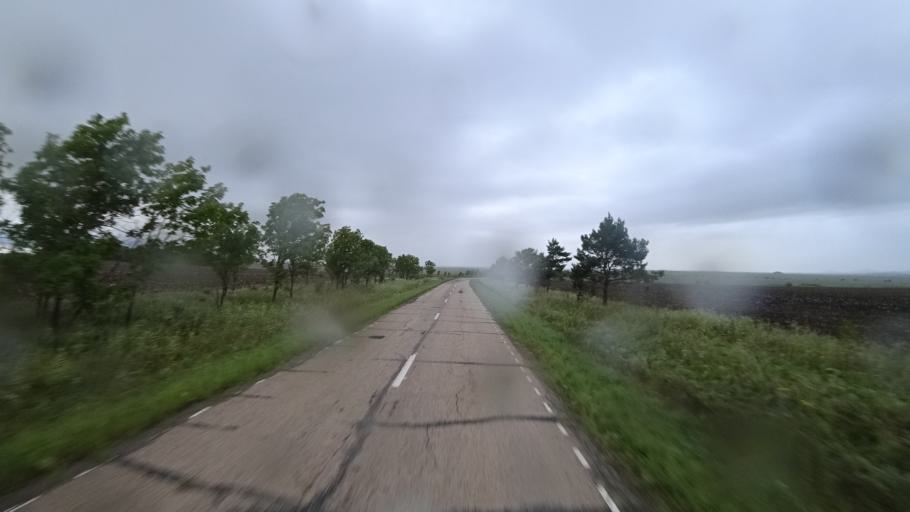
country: RU
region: Primorskiy
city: Chernigovka
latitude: 44.3700
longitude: 132.5314
